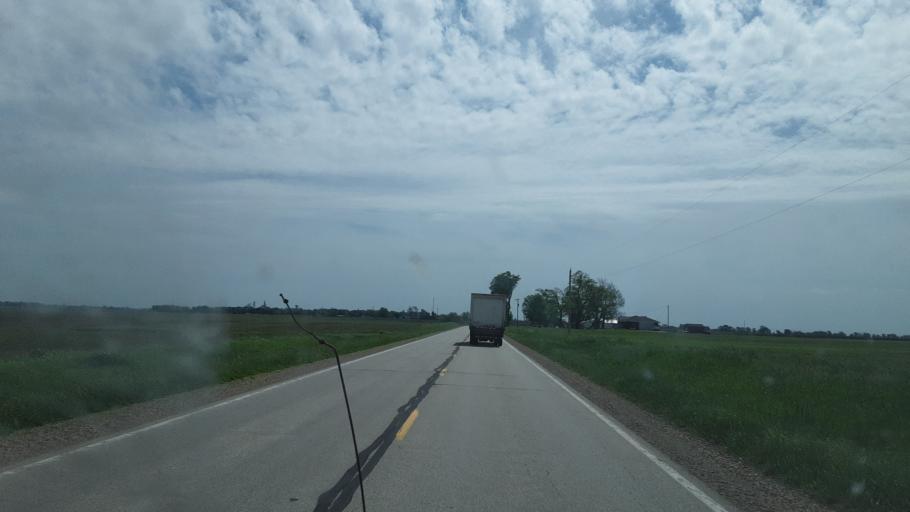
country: US
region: Illinois
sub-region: Logan County
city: Atlanta
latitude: 40.3114
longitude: -89.1999
